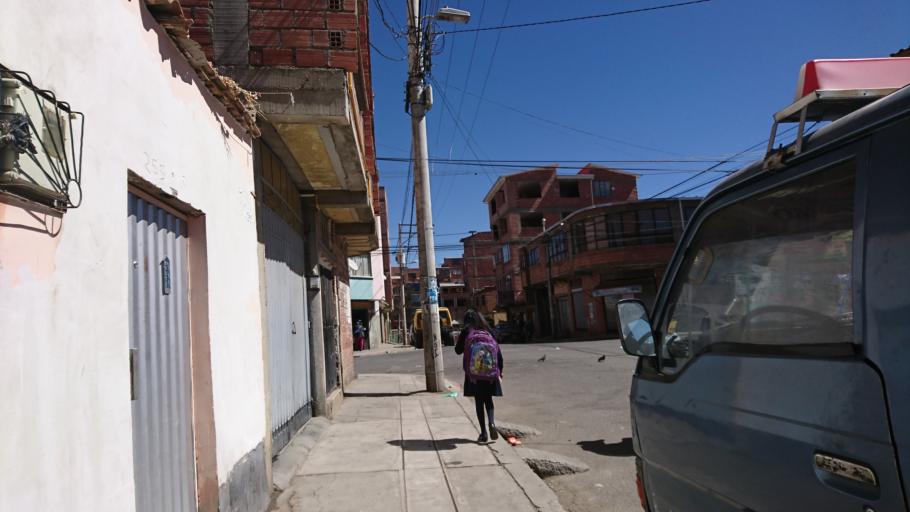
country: BO
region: La Paz
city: La Paz
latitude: -16.5009
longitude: -68.1037
